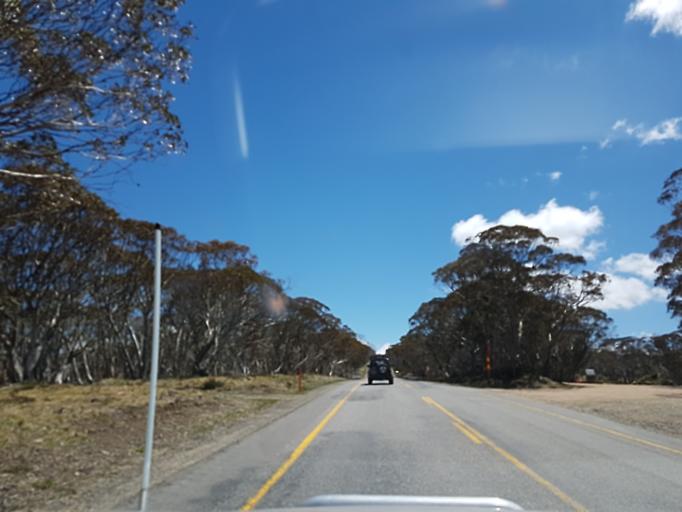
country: AU
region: Victoria
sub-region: Alpine
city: Mount Beauty
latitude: -37.0046
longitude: 147.1836
